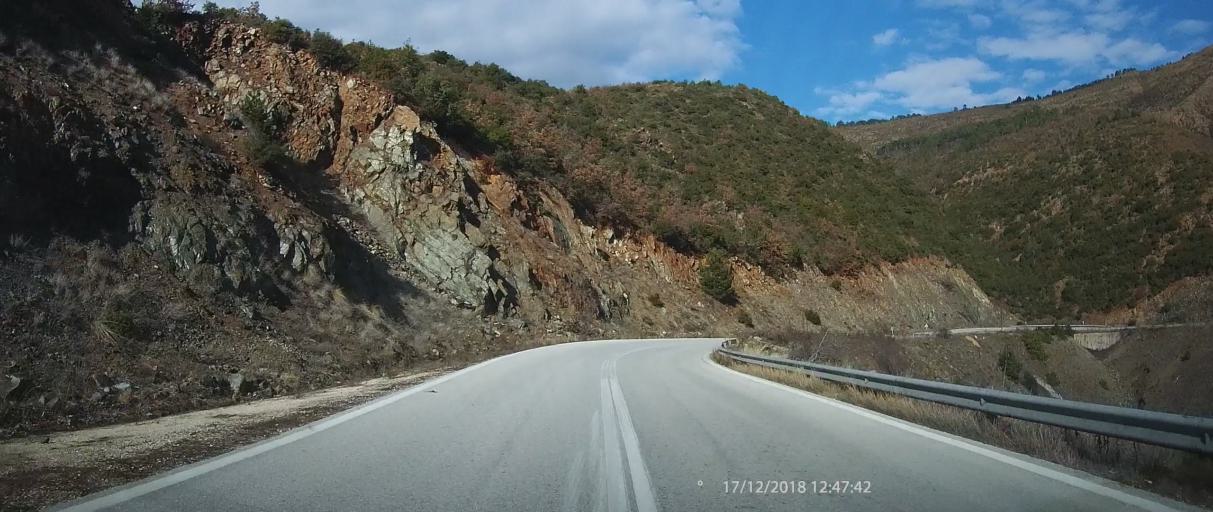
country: GR
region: Thessaly
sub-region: Trikala
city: Kastraki
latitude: 39.7844
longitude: 21.4308
